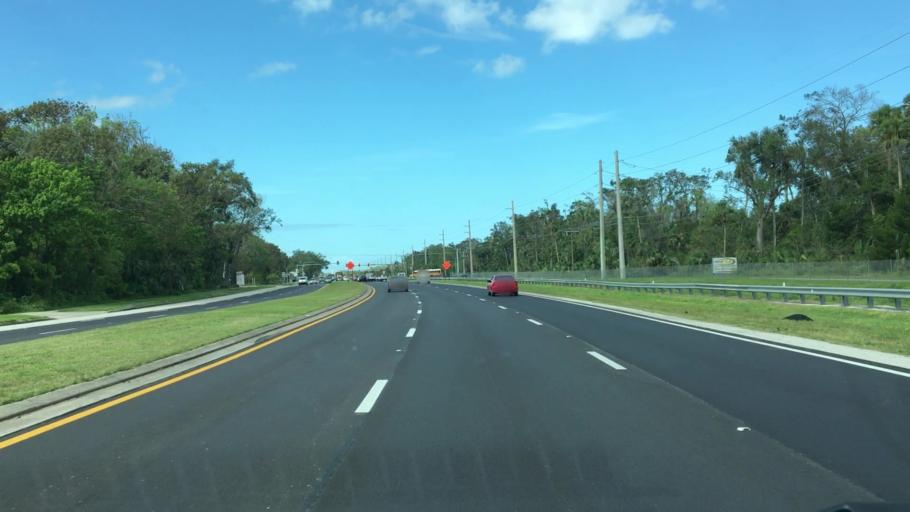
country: US
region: Florida
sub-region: Volusia County
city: Daytona Beach
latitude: 29.1868
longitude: -81.0306
